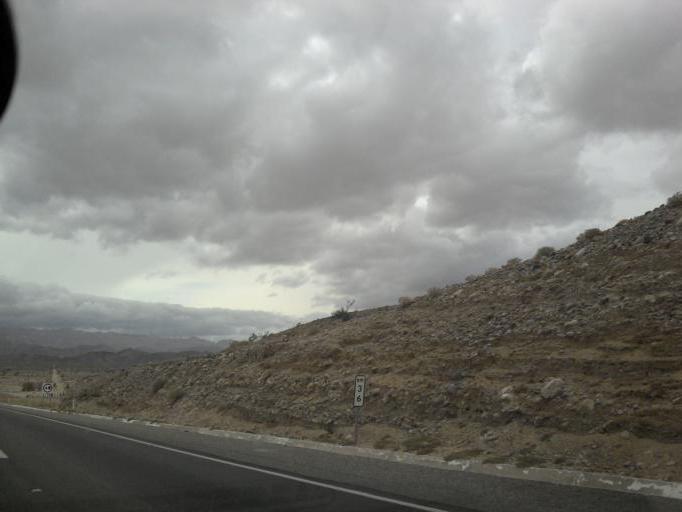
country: MX
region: Baja California
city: Progreso
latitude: 32.5646
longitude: -115.8761
